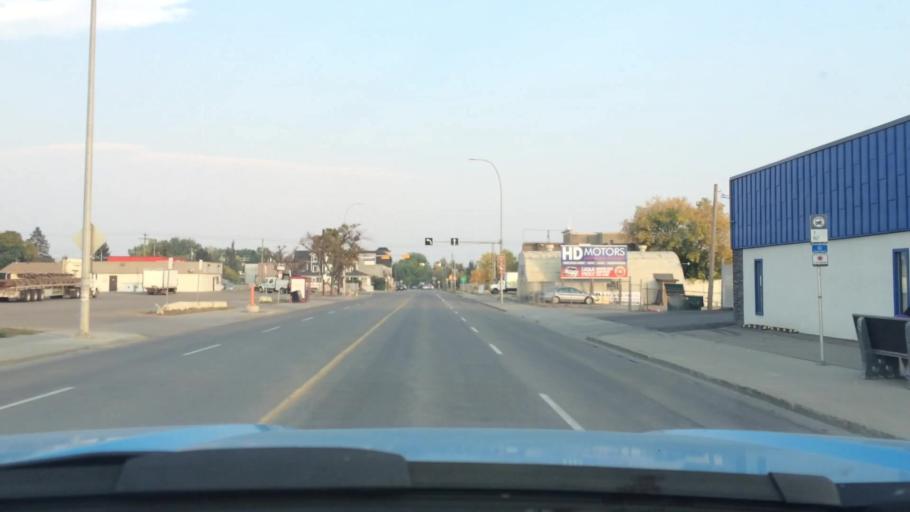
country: CA
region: Alberta
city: Calgary
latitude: 51.0362
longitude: -114.0218
